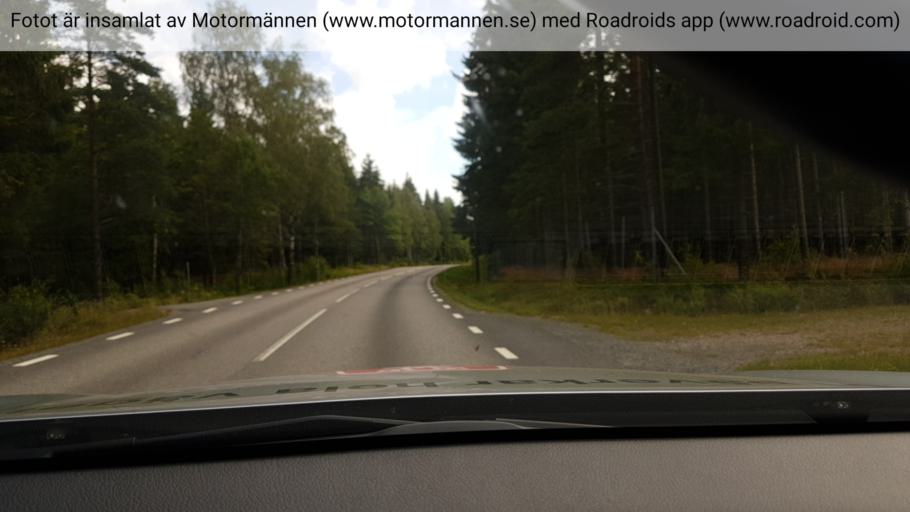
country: SE
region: Vaestra Goetaland
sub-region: Marks Kommun
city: Fritsla
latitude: 57.4815
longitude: 12.8057
